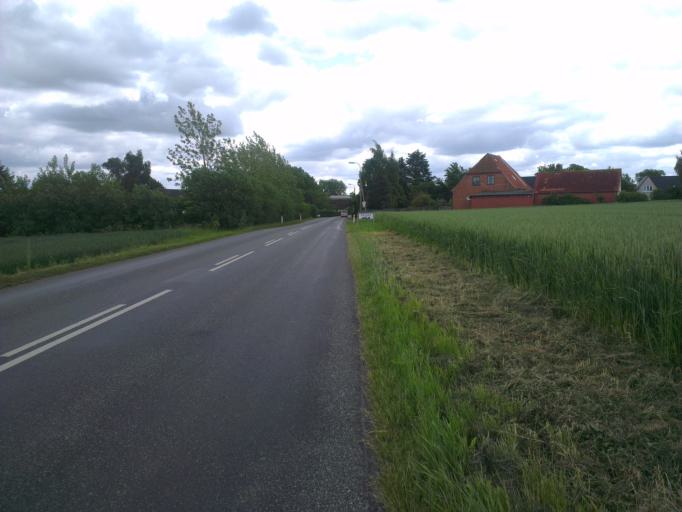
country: DK
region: Capital Region
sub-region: Frederikssund Kommune
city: Frederikssund
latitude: 55.8122
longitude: 12.0214
